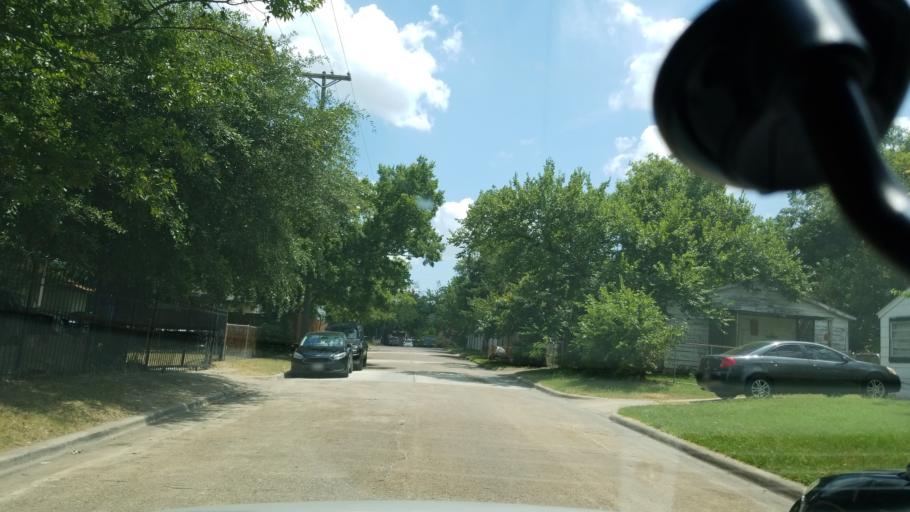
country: US
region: Texas
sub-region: Dallas County
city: Cockrell Hill
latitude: 32.7272
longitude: -96.8793
